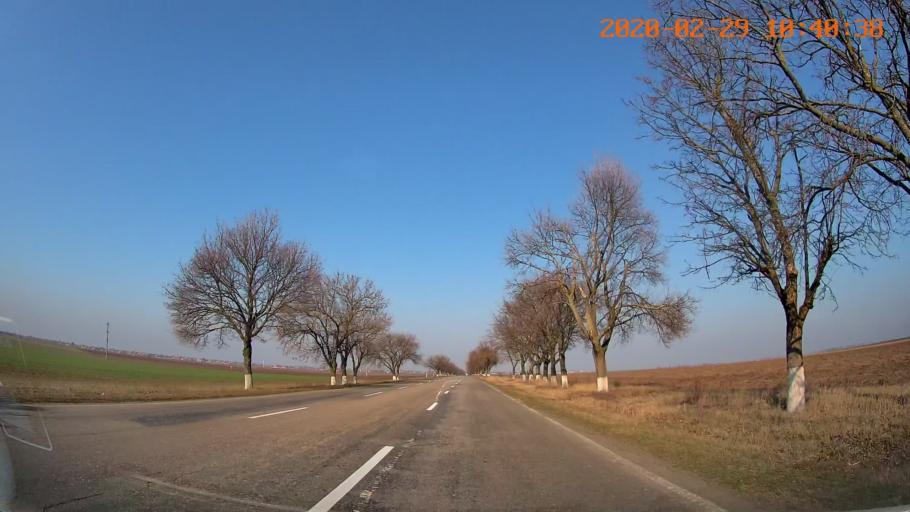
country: MD
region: Anenii Noi
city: Varnita
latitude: 47.0349
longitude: 29.4367
